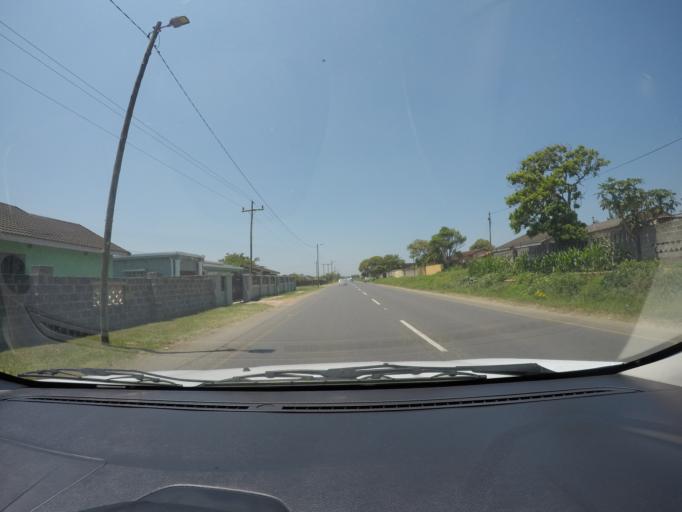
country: ZA
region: KwaZulu-Natal
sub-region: uThungulu District Municipality
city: eSikhawini
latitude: -28.8835
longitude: 31.8874
